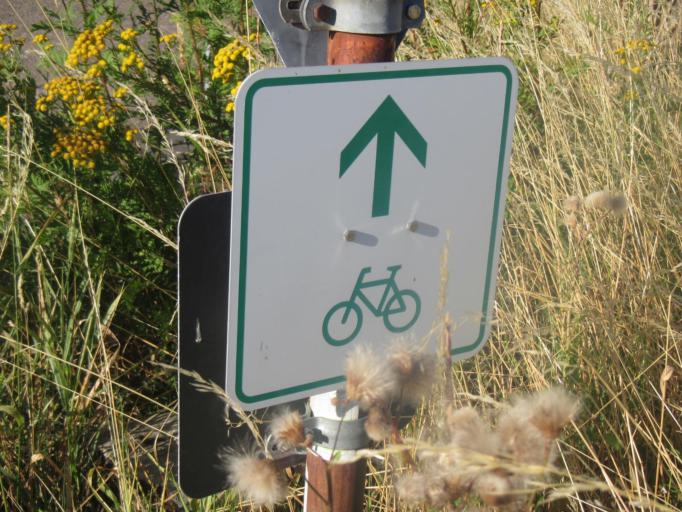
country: DE
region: Rheinland-Pfalz
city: Eschbach
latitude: 49.1770
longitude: 8.0194
